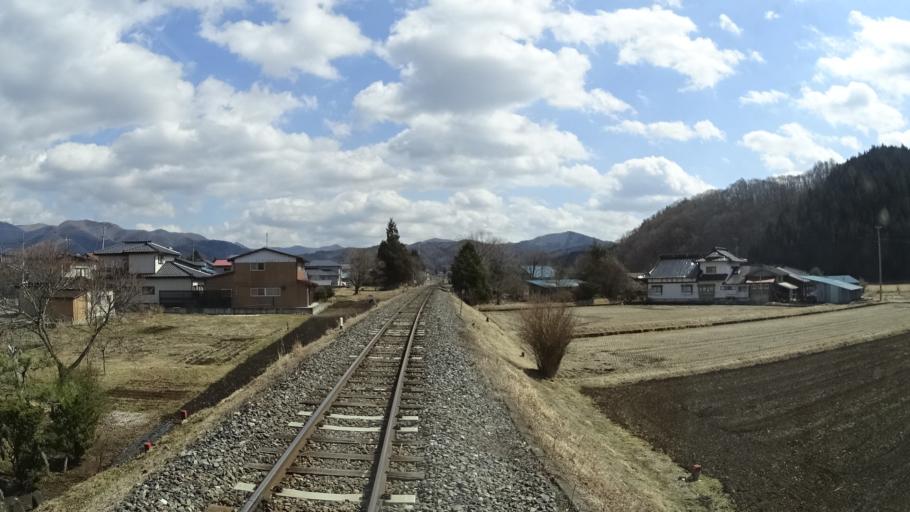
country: JP
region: Iwate
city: Tono
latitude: 39.2865
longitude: 141.5839
